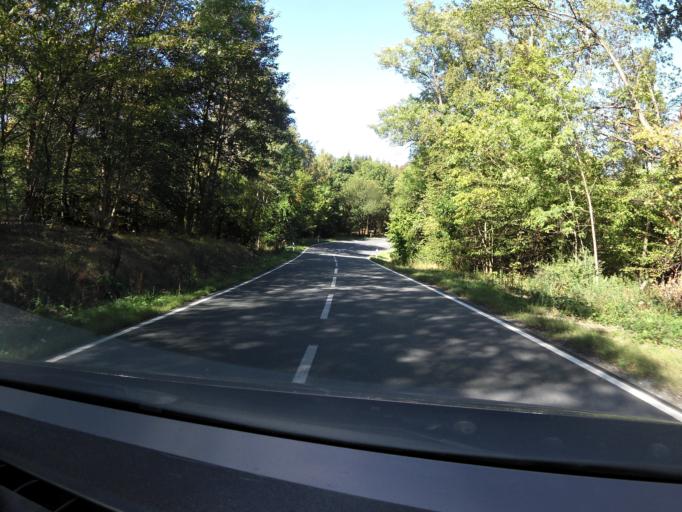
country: DE
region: Saxony-Anhalt
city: Gernrode
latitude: 51.7027
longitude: 11.1302
